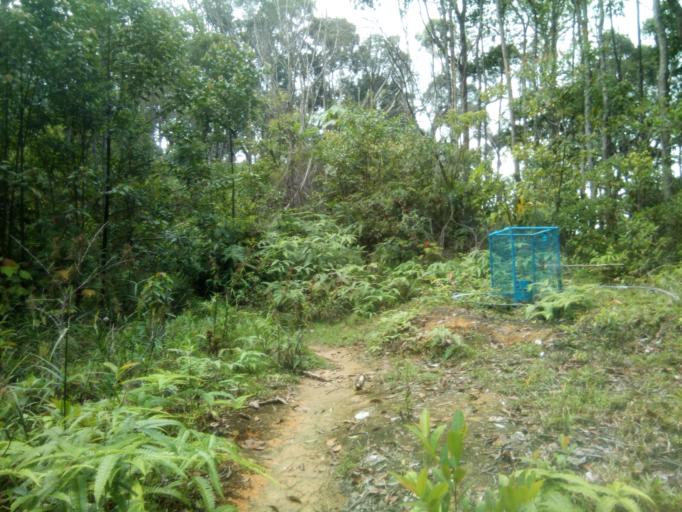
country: MY
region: Penang
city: Tanjung Tokong
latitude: 5.4274
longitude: 100.2830
